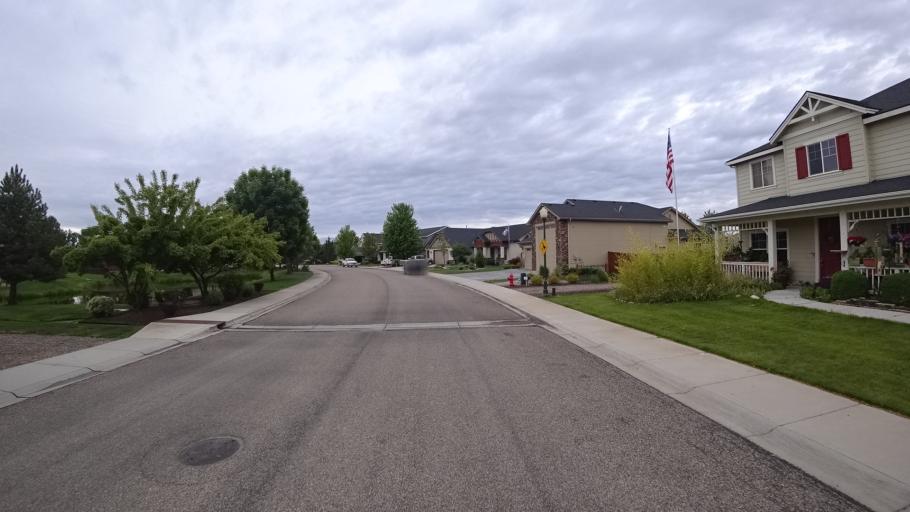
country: US
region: Idaho
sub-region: Ada County
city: Star
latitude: 43.7011
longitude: -116.4805
